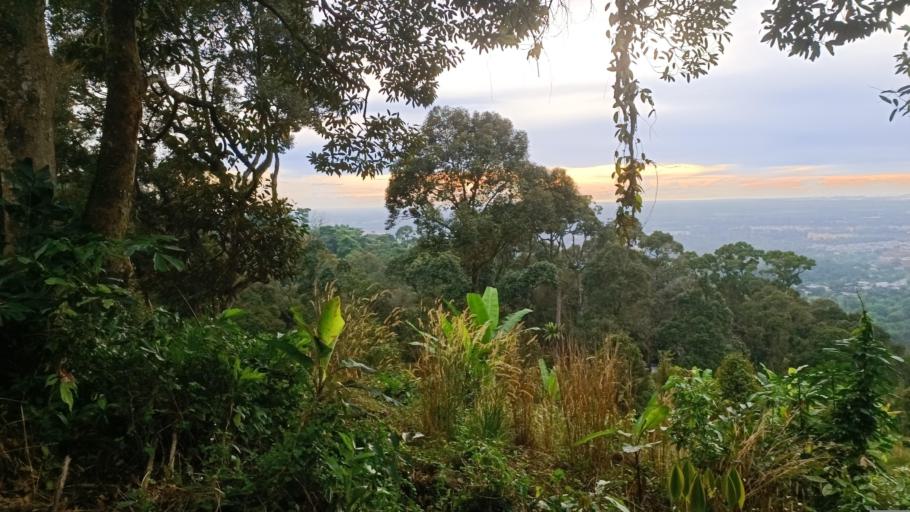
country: MY
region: Penang
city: Nibong Tebal
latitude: 5.2333
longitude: 100.5112
